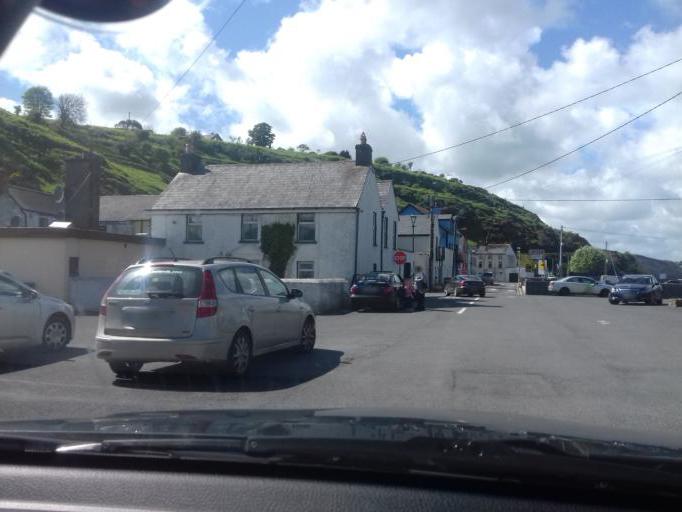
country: IE
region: Munster
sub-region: Waterford
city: Dunmore East
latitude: 52.2391
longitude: -6.9716
